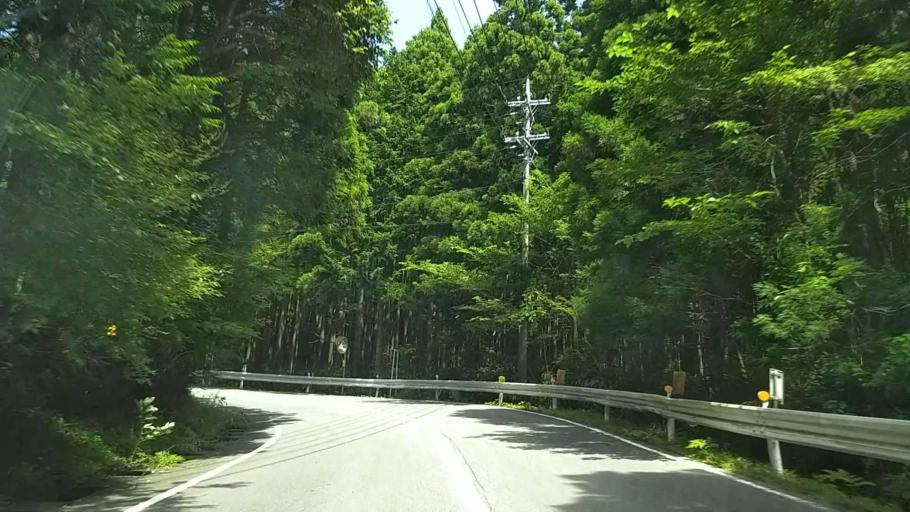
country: JP
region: Shizuoka
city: Gotemba
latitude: 35.2578
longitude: 138.8250
